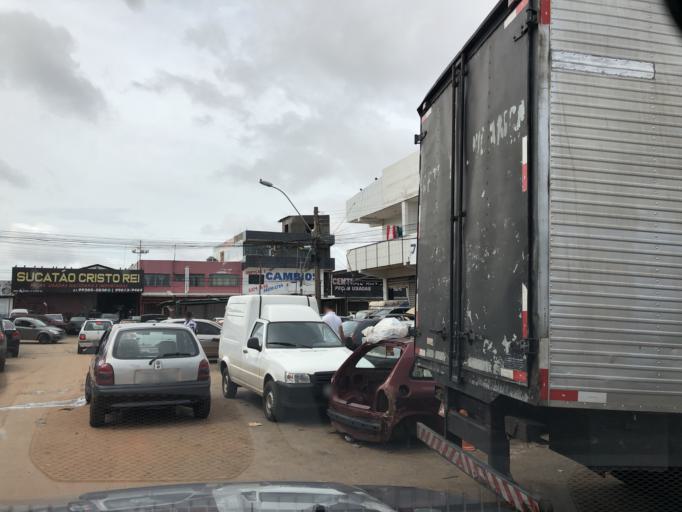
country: BR
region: Federal District
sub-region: Brasilia
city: Brasilia
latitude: -15.8016
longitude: -48.1299
